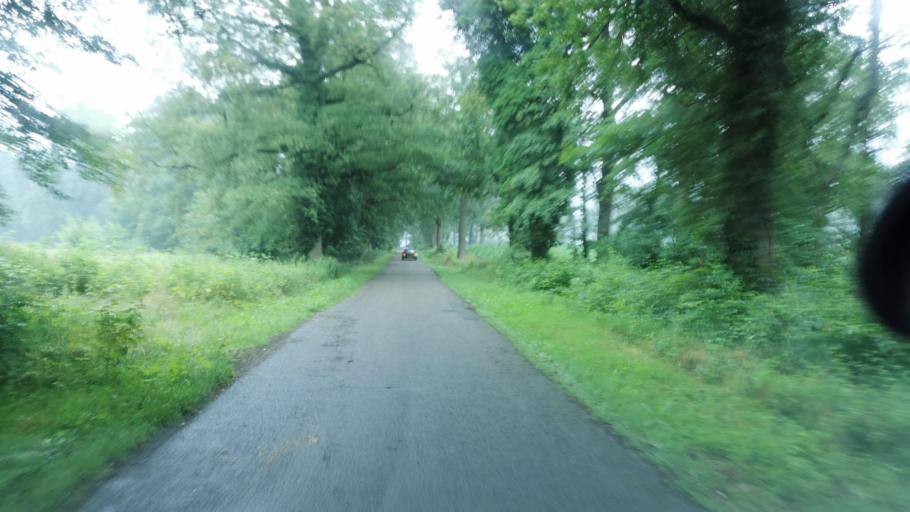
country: NL
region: Overijssel
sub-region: Gemeente Losser
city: Losser
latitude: 52.2427
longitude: 6.9648
